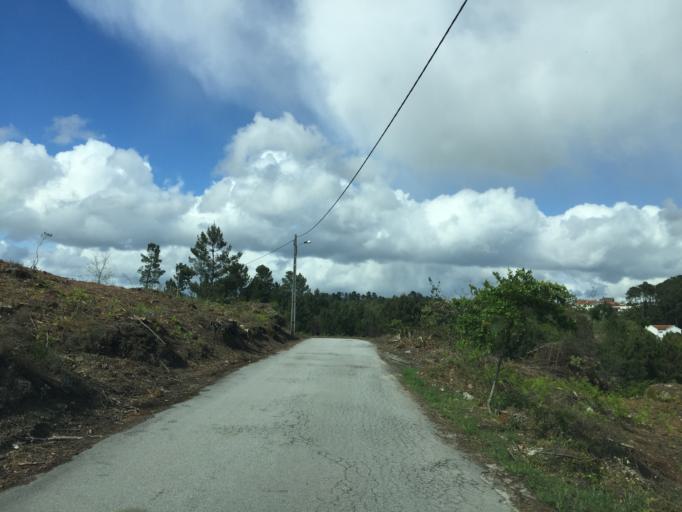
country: PT
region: Viseu
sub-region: Viseu
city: Abraveses
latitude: 40.6571
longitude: -7.9471
